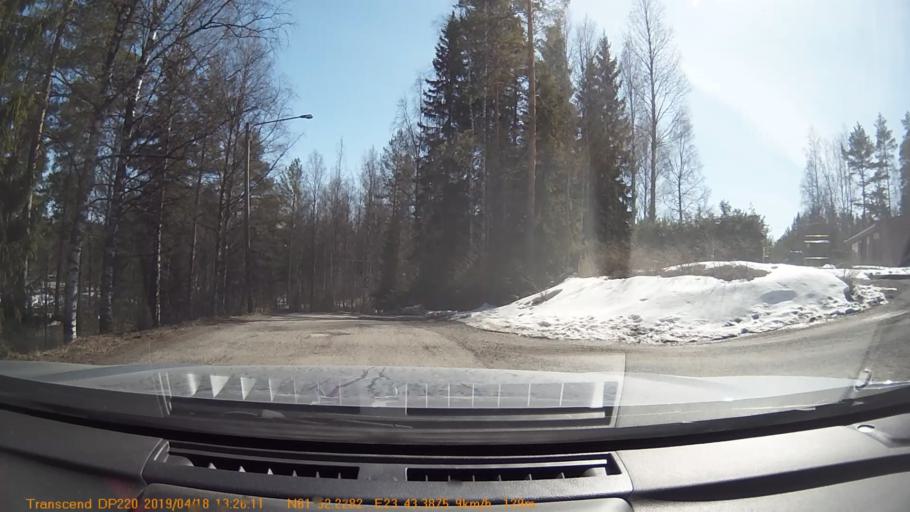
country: FI
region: Pirkanmaa
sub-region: Tampere
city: Kuru
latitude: 61.8705
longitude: 23.7231
